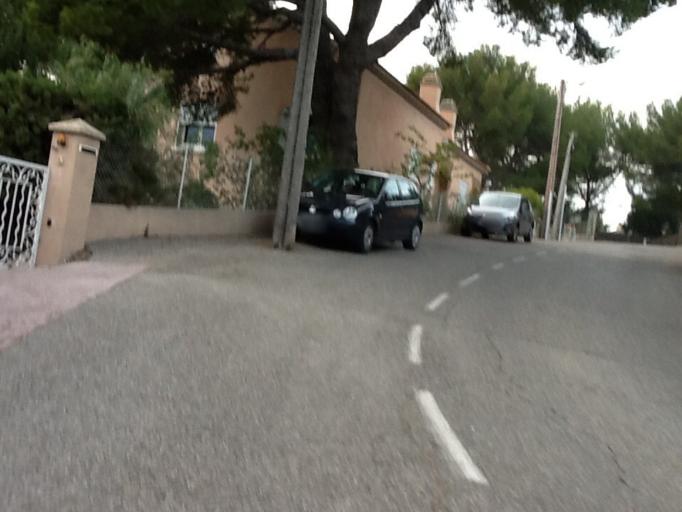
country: FR
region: Provence-Alpes-Cote d'Azur
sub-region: Departement du Var
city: Sanary-sur-Mer
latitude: 43.1101
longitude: 5.8177
